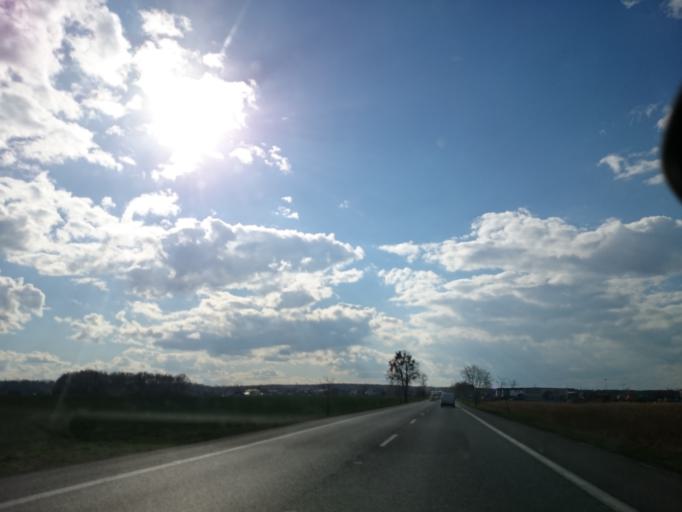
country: PL
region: Opole Voivodeship
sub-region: Powiat opolski
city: Dabrowa
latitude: 50.6898
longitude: 17.7703
